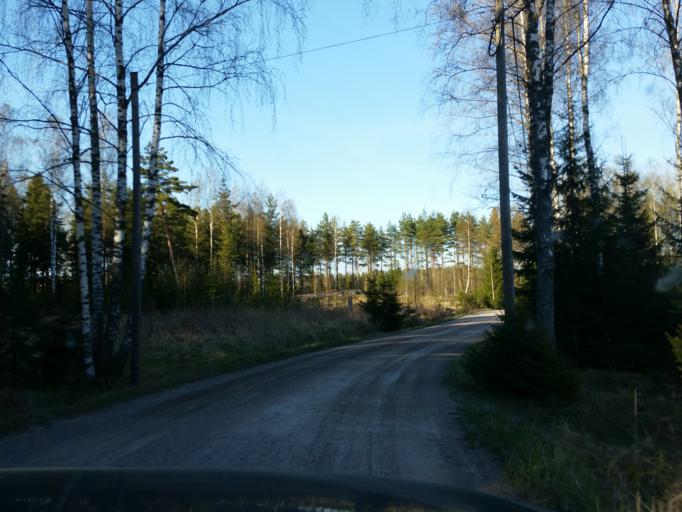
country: FI
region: Uusimaa
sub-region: Helsinki
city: Espoo
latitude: 60.1104
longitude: 24.6174
